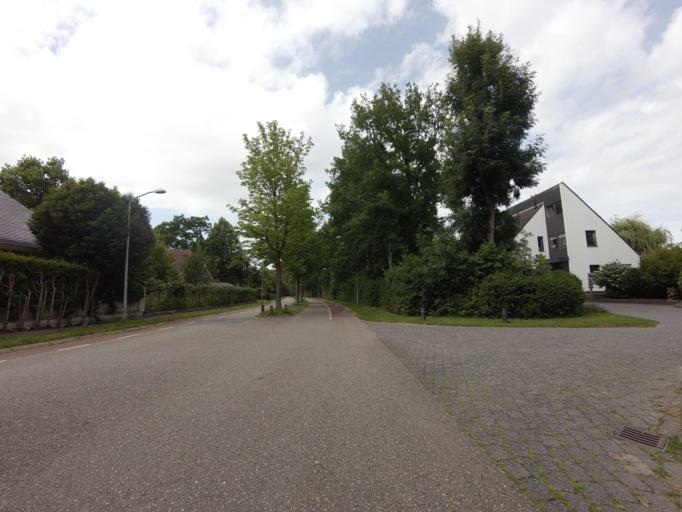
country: NL
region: North Holland
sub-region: Gemeente Huizen
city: Huizen
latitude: 52.3423
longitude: 5.2997
